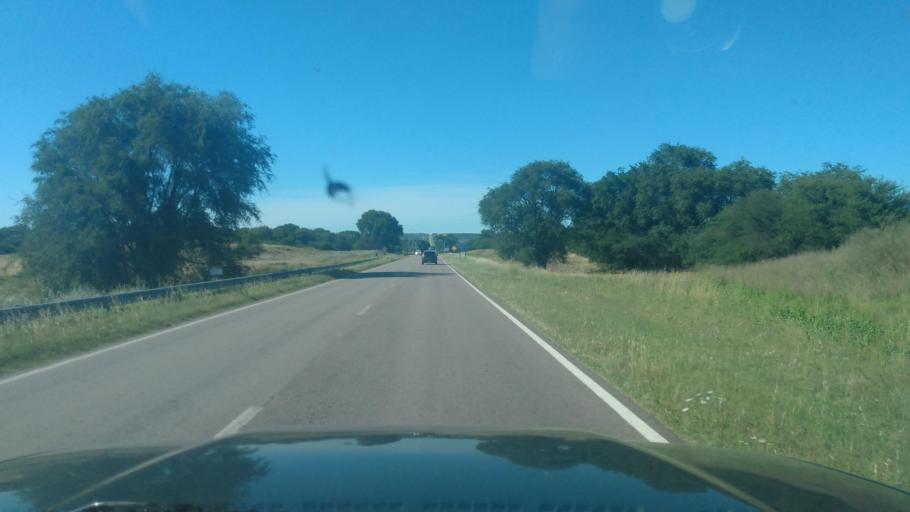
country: AR
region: La Pampa
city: Doblas
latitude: -37.3012
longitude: -64.2878
